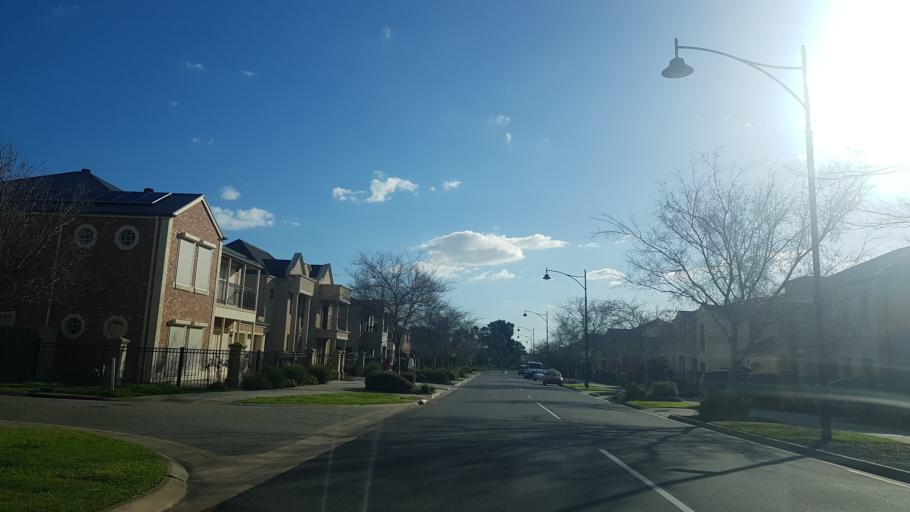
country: AU
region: South Australia
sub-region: Salisbury
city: Ingle Farm
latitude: -34.8178
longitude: 138.6108
